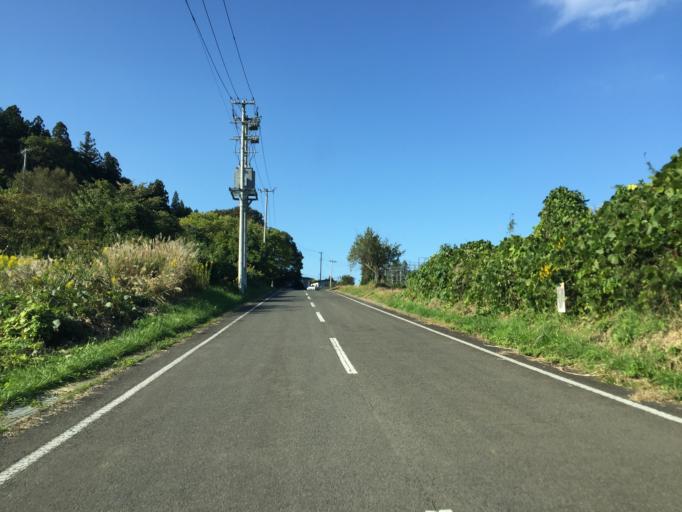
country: JP
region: Fukushima
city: Fukushima-shi
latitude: 37.6624
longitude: 140.4857
